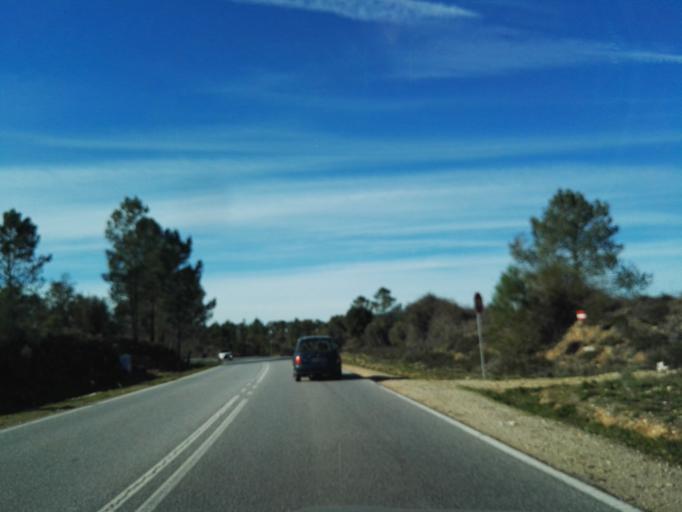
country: PT
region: Santarem
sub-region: Abrantes
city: Alferrarede
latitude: 39.4739
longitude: -8.0720
